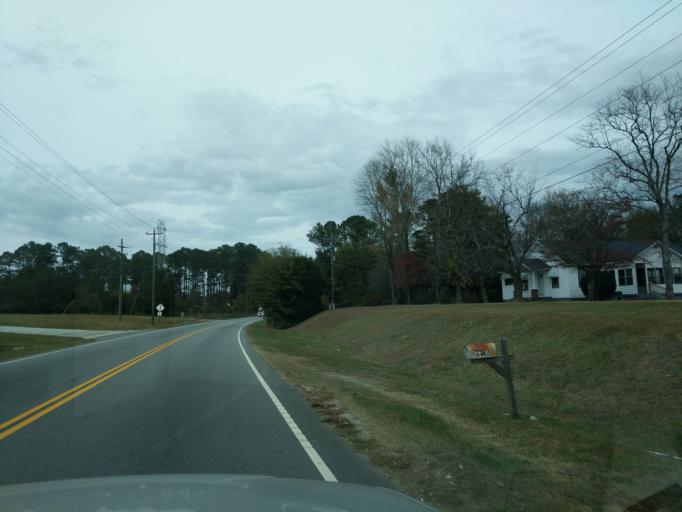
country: US
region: South Carolina
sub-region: Newberry County
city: Newberry
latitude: 34.2481
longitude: -81.6436
